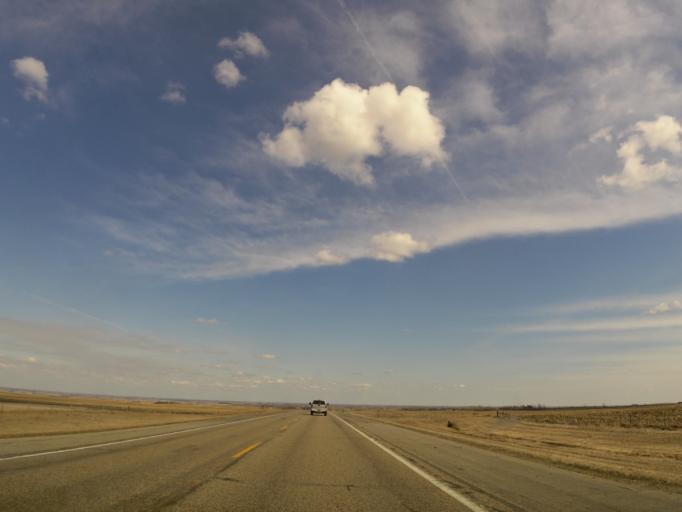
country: US
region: South Dakota
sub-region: Deuel County
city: Clear Lake
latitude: 44.9332
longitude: -96.5911
